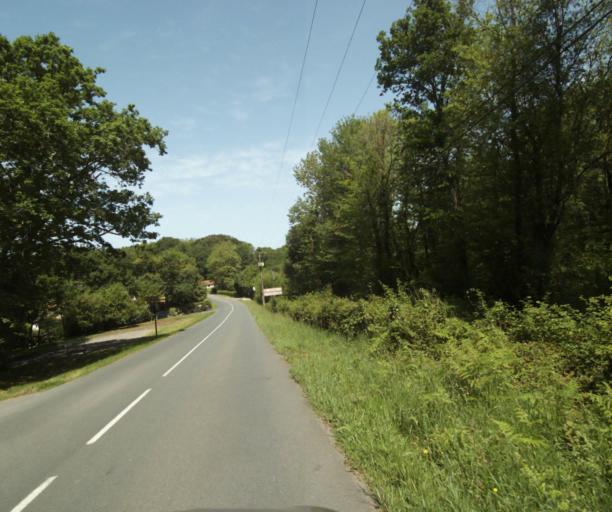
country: FR
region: Aquitaine
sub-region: Departement des Pyrenees-Atlantiques
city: Mouguerre
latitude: 43.4532
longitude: -1.4256
